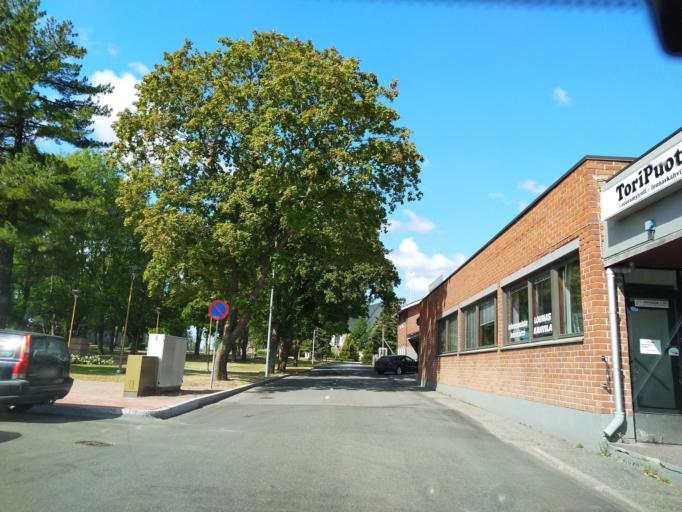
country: FI
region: Satakunta
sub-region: Pori
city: Huittinen
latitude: 61.1800
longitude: 22.6964
